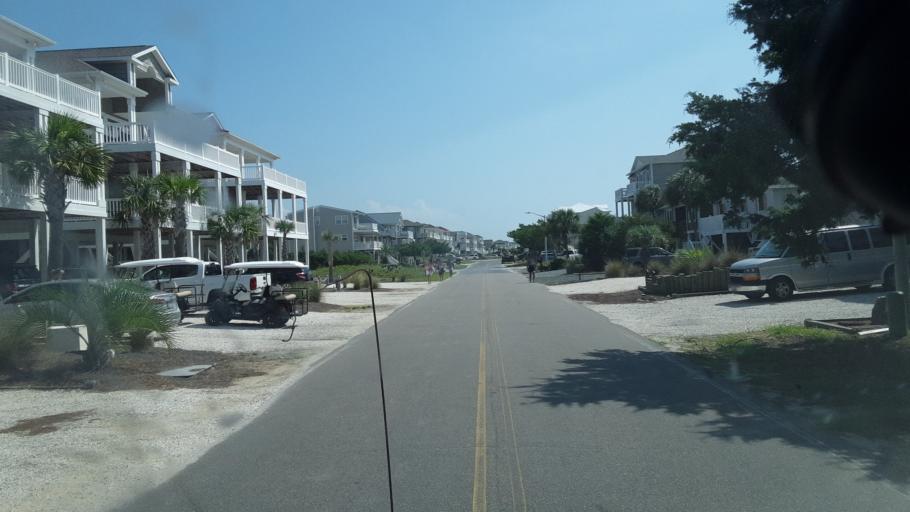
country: US
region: North Carolina
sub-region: Brunswick County
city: Shallotte
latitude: 33.8944
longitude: -78.4098
